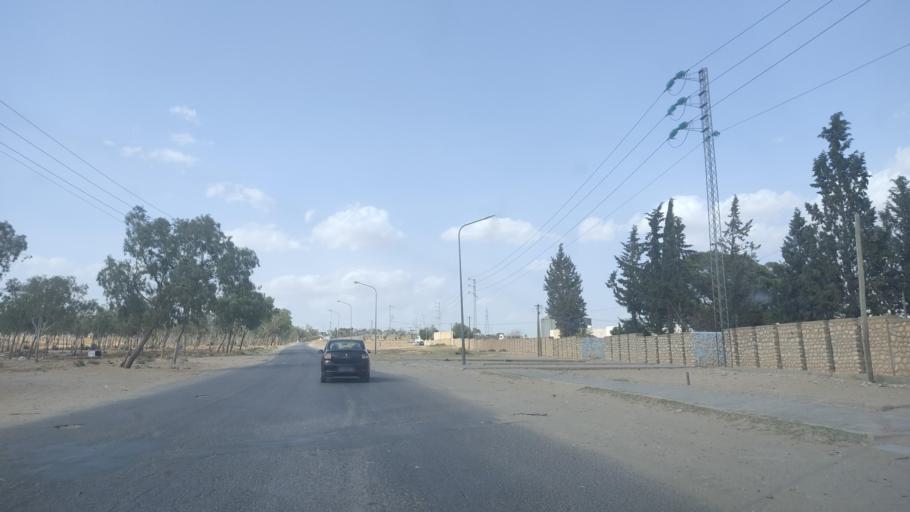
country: TN
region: Sidi Bu Zayd
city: Sidi Bouzid
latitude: 35.1056
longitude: 9.5374
